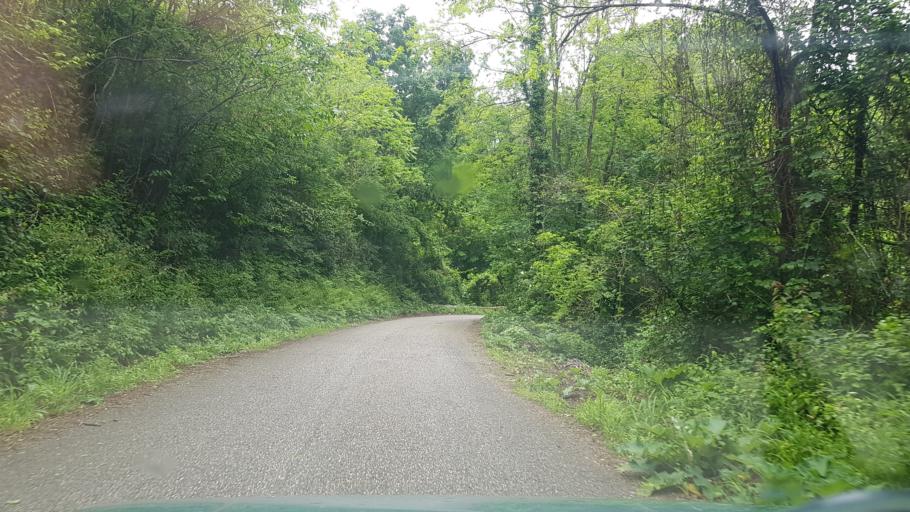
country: IT
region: Friuli Venezia Giulia
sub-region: Provincia di Gorizia
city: San Floriano del Collio
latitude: 45.9518
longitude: 13.5941
